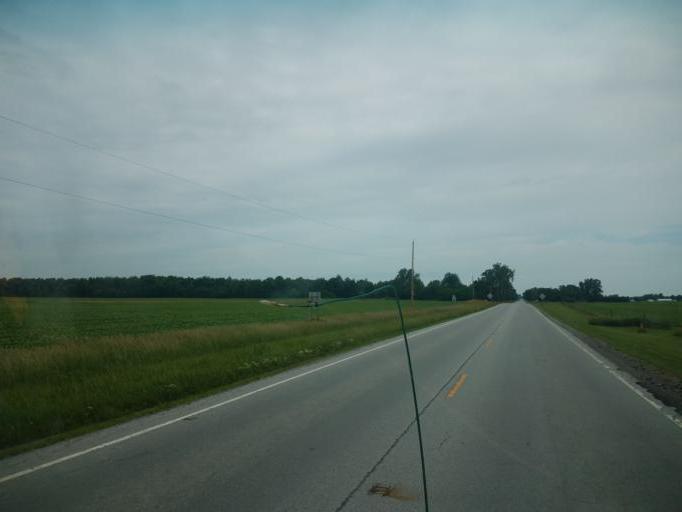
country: US
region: Ohio
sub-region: Hardin County
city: Ada
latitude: 40.7345
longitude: -83.8232
